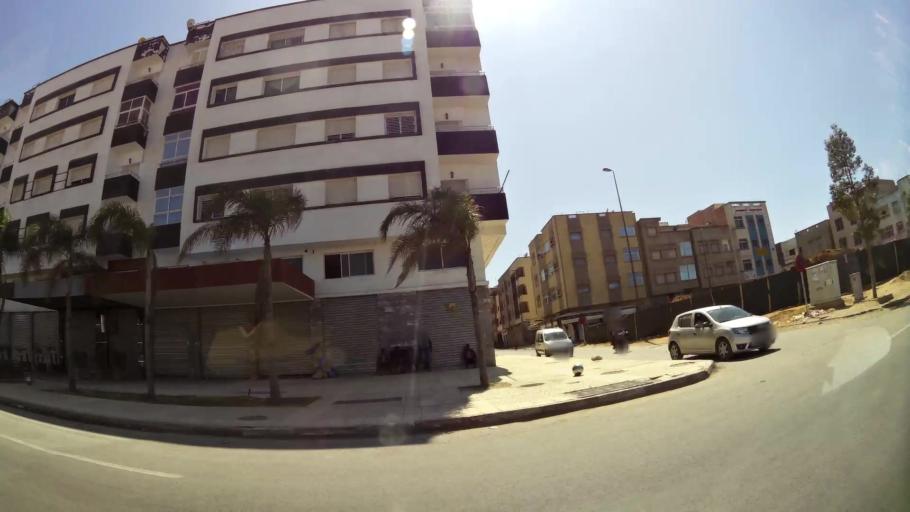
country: MA
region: Gharb-Chrarda-Beni Hssen
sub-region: Kenitra Province
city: Kenitra
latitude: 34.2405
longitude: -6.5478
